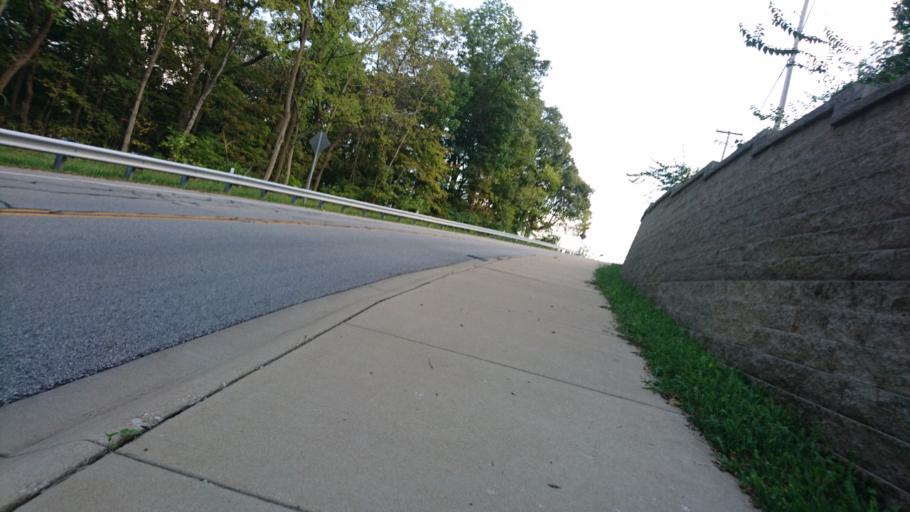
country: US
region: Missouri
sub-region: Saint Louis County
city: Eureka
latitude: 38.5137
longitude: -90.6325
